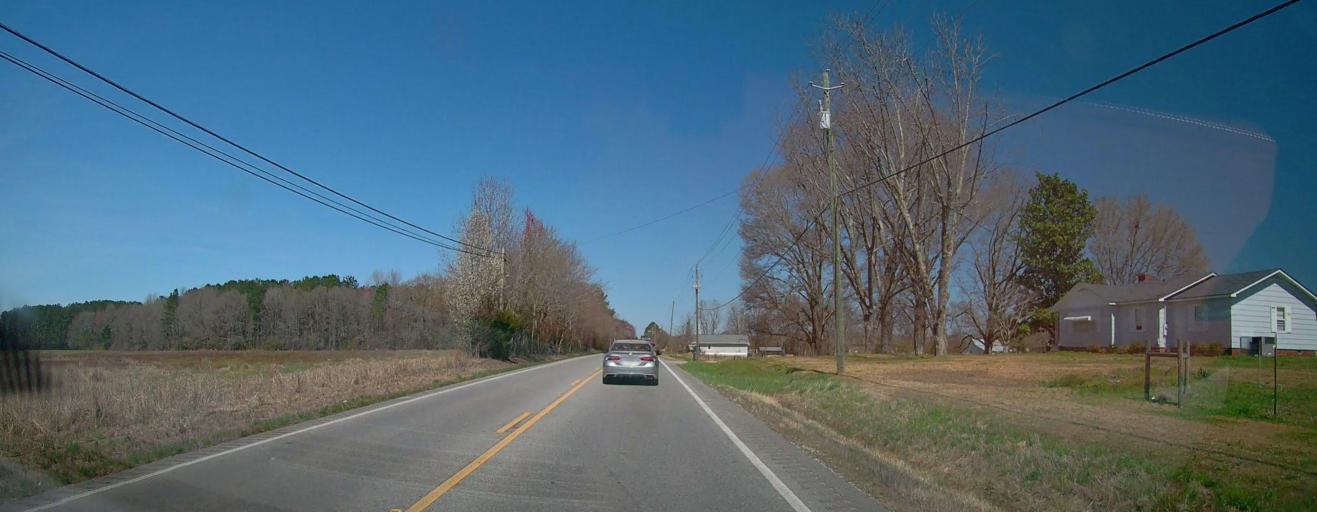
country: US
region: Alabama
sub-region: Etowah County
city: Southside
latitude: 33.8890
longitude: -86.0308
